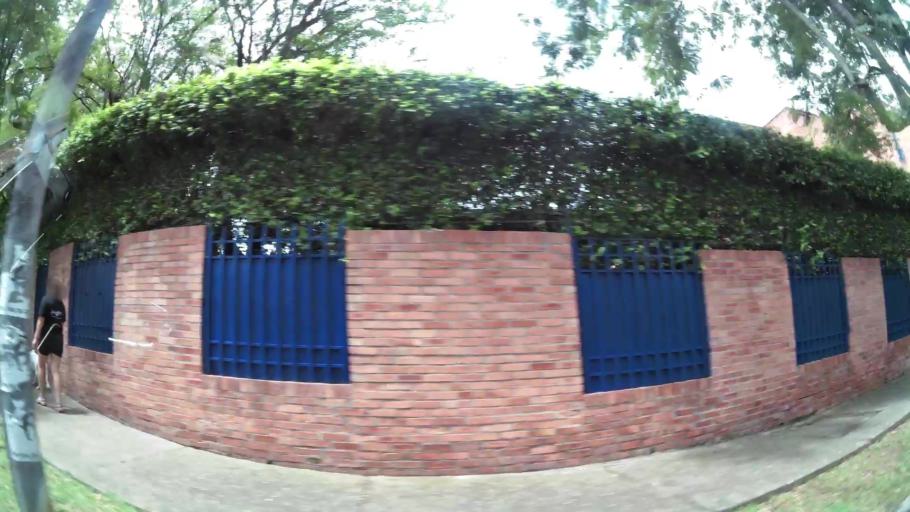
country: CO
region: Valle del Cauca
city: Cali
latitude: 3.3804
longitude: -76.5332
